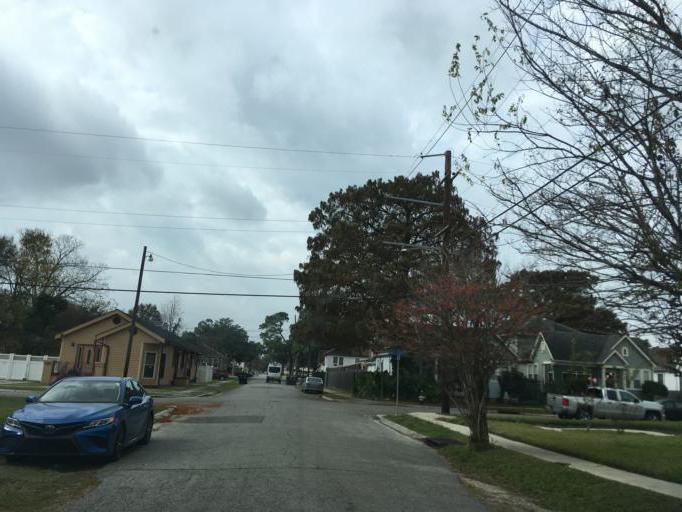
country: US
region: Louisiana
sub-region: Orleans Parish
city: New Orleans
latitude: 29.9950
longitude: -90.0573
